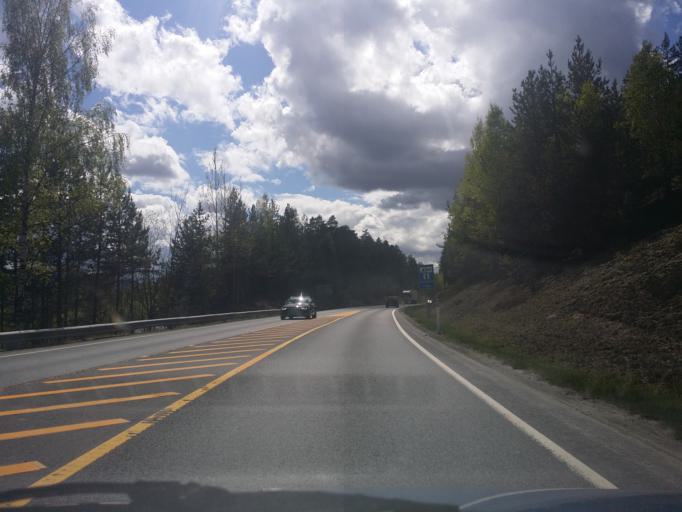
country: NO
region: Buskerud
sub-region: Modum
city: Vikersund
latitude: 59.9427
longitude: 9.9663
